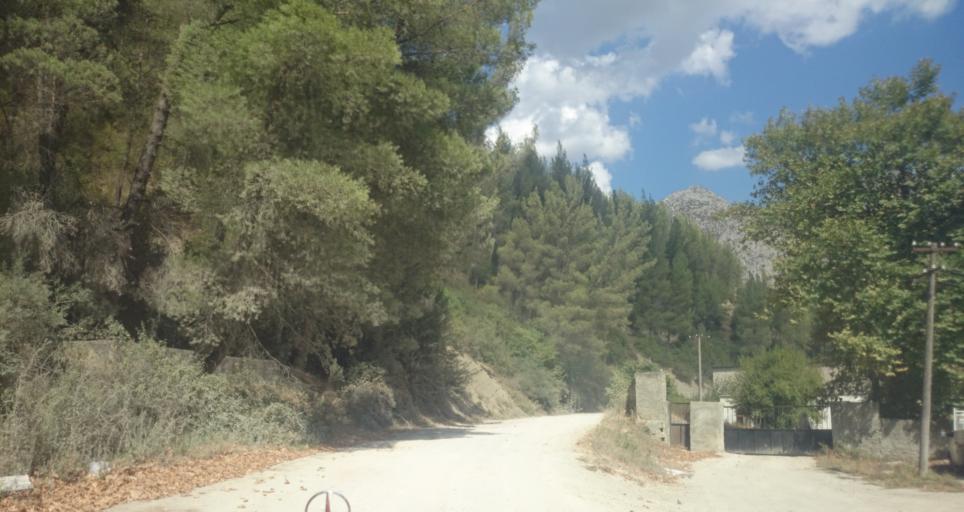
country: AL
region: Berat
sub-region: Rrethi i Skraparit
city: Corovode
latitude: 40.5155
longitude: 20.2381
